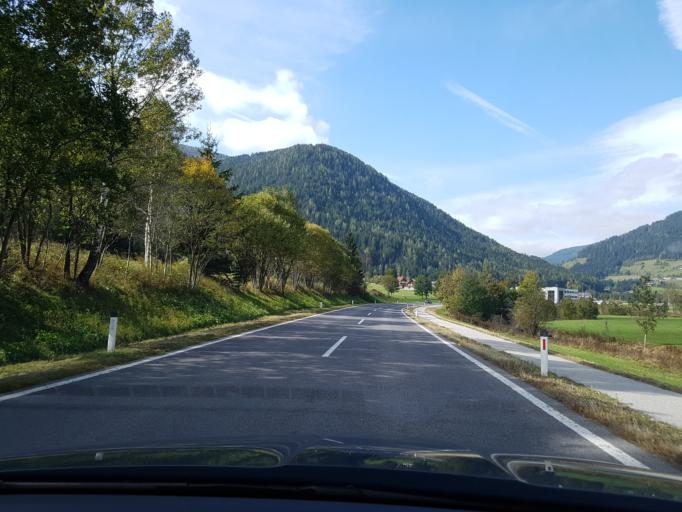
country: AT
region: Carinthia
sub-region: Politischer Bezirk Villach Land
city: Arriach
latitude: 46.8089
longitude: 13.8776
